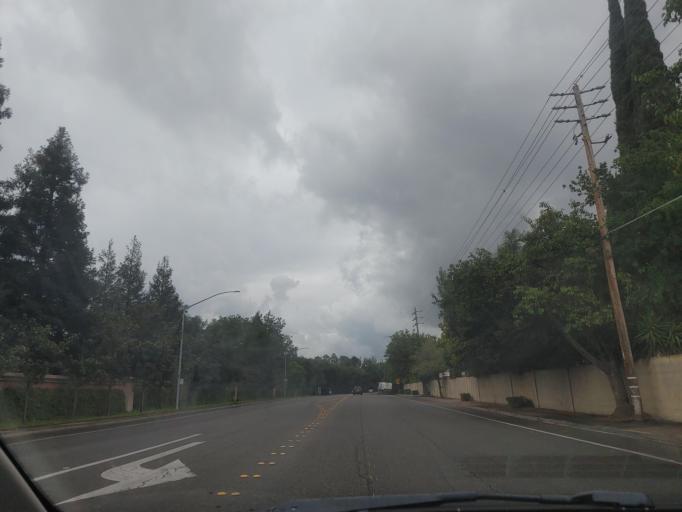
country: US
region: California
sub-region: Stanislaus County
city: Empire
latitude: 37.6538
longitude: -120.9442
